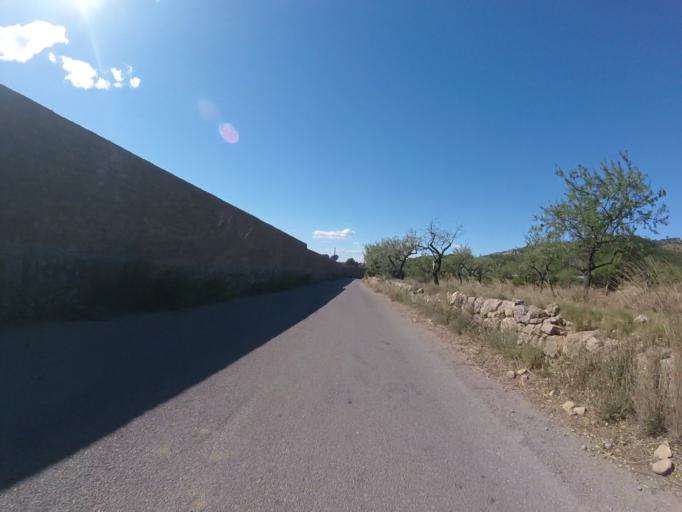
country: ES
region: Valencia
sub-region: Provincia de Castello
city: Benicassim
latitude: 40.0679
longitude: 0.0744
